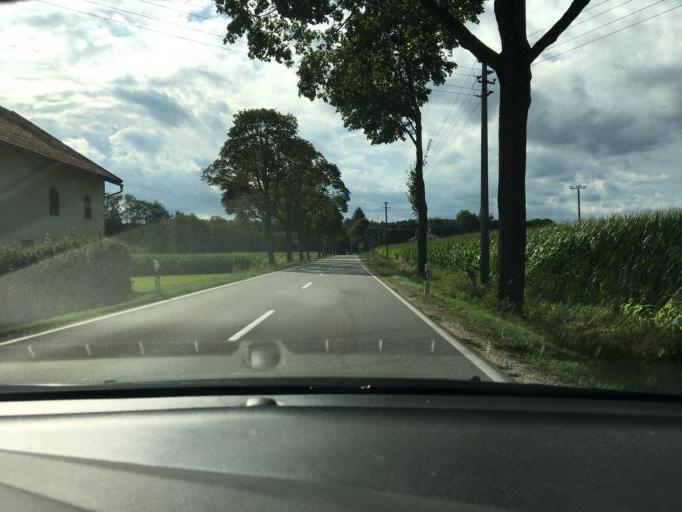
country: DE
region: Bavaria
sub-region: Upper Bavaria
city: Bockhorn
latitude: 48.2914
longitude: 11.9809
